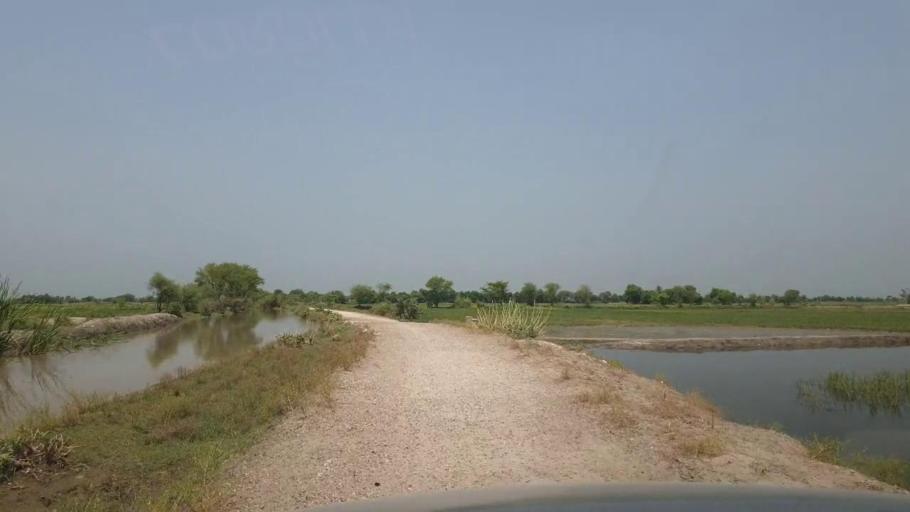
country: PK
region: Sindh
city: Garhi Yasin
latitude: 27.8379
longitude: 68.4901
